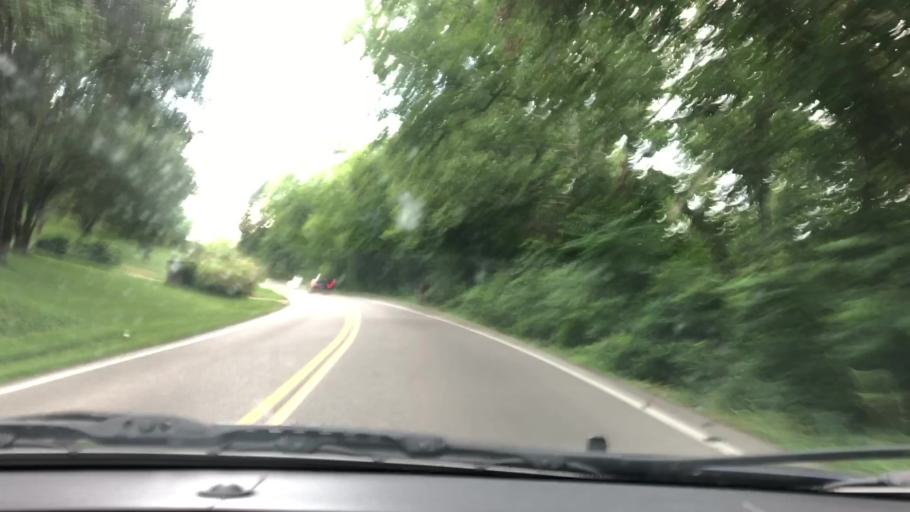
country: US
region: Tennessee
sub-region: Maury County
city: Columbia
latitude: 35.6957
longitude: -87.0111
